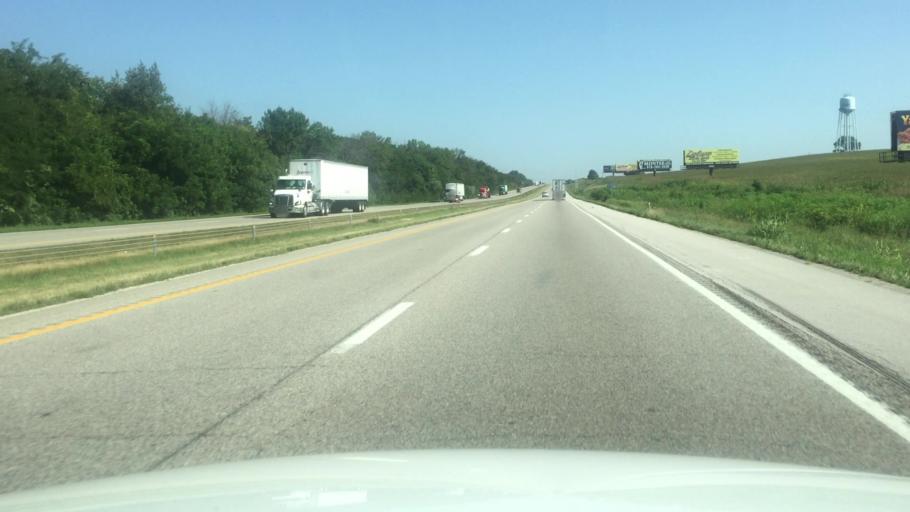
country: US
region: Missouri
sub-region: Platte County
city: Platte City
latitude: 39.5208
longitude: -94.7869
